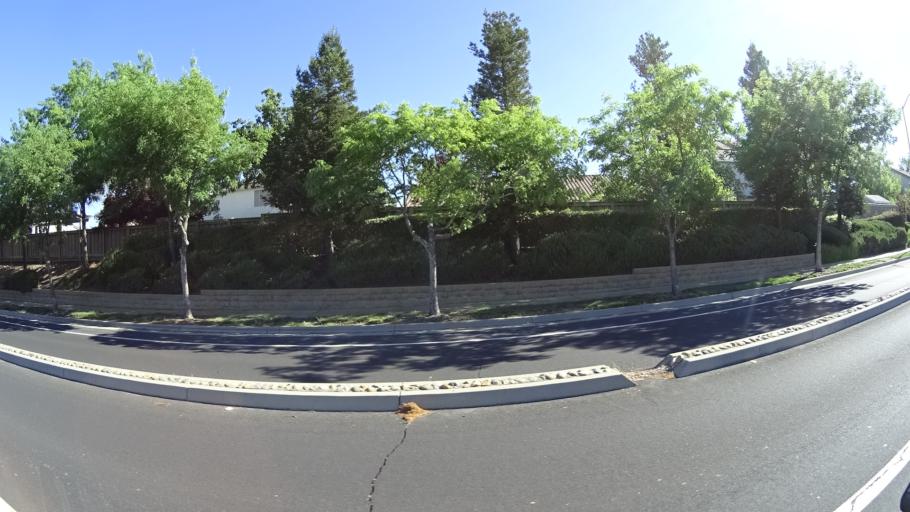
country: US
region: California
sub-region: Placer County
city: Rocklin
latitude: 38.7902
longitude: -121.2751
